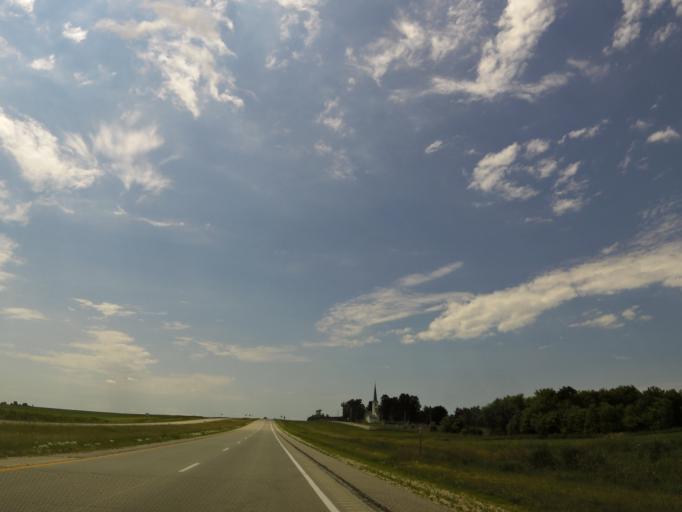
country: US
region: Iowa
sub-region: Bremer County
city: Denver
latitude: 42.7590
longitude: -92.3365
